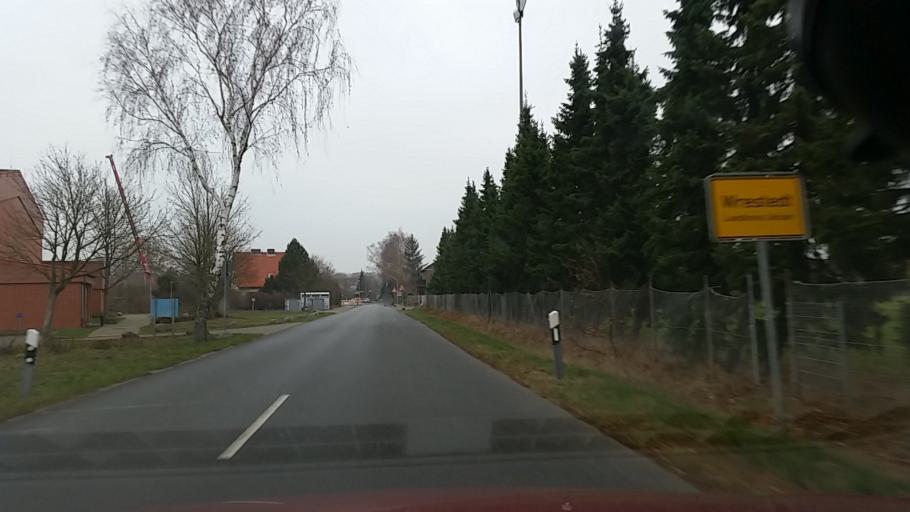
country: DE
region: Lower Saxony
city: Wrestedt
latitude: 52.9050
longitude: 10.5902
